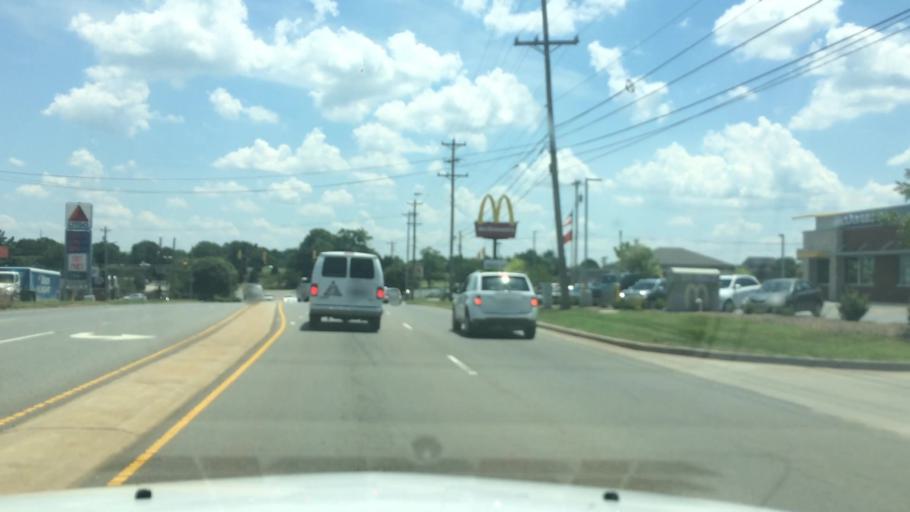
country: US
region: North Carolina
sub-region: Iredell County
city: Statesville
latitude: 35.7964
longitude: -80.9387
